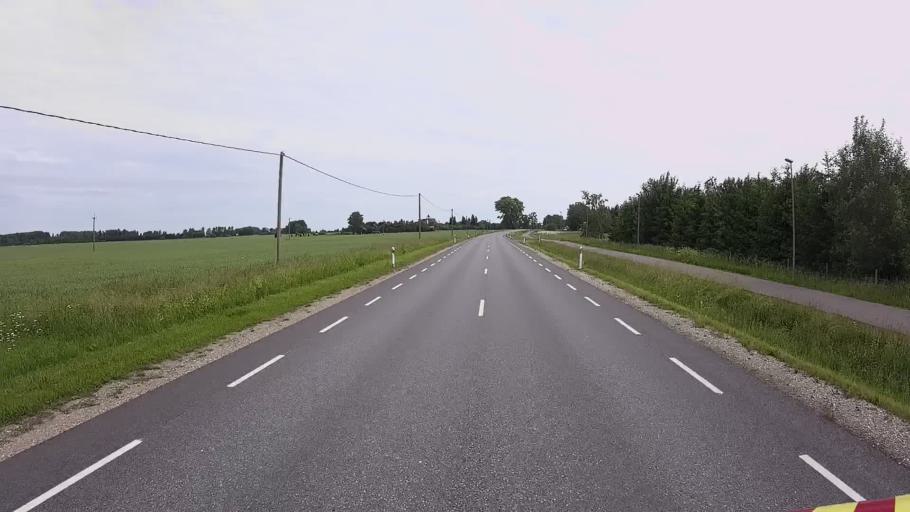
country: EE
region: Viljandimaa
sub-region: Karksi vald
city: Karksi-Nuia
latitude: 58.1141
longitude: 25.5733
